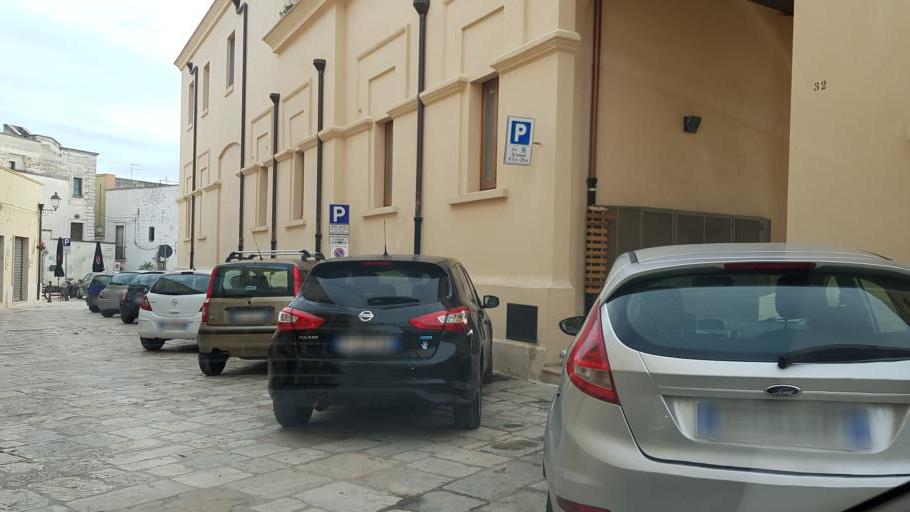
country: IT
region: Apulia
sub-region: Provincia di Brindisi
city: Mesagne
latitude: 40.5589
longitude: 17.8089
